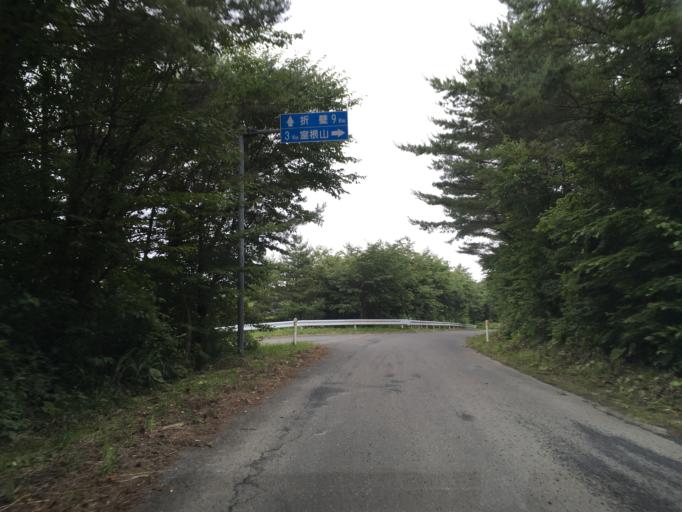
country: JP
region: Iwate
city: Ofunato
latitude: 38.9832
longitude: 141.4533
